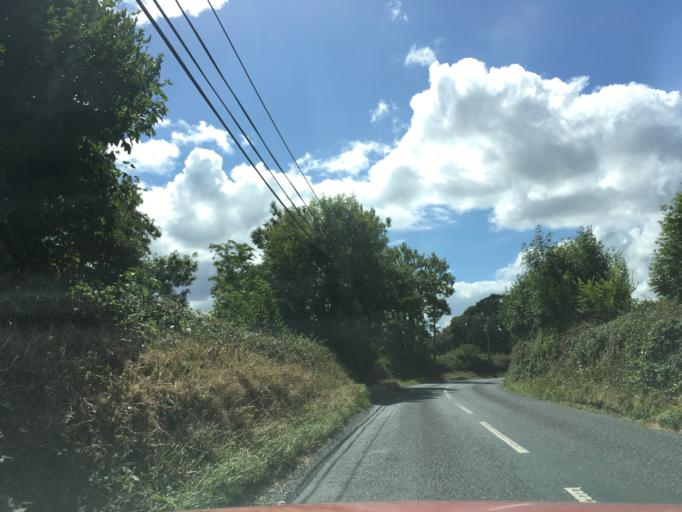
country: IE
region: Munster
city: Cahir
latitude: 52.3475
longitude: -7.9397
